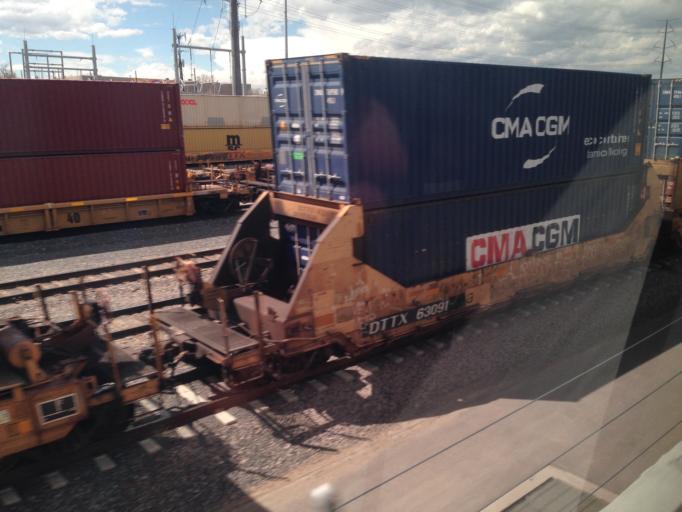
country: US
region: Colorado
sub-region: Denver County
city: Denver
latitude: 39.7758
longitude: -104.9971
